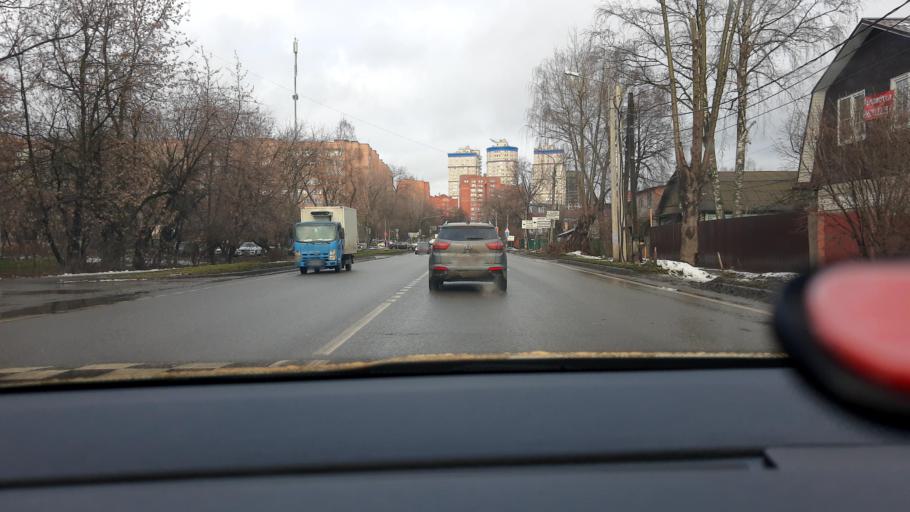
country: RU
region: Moskovskaya
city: Pushkino
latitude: 55.9940
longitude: 37.8676
